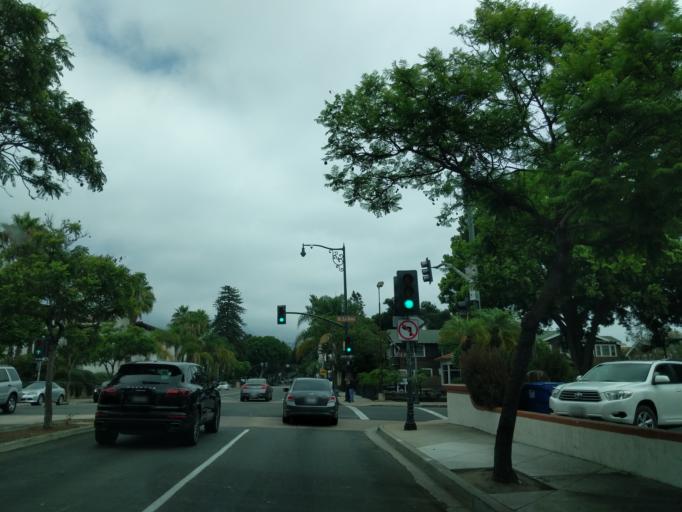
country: US
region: California
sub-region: Santa Barbara County
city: Santa Barbara
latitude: 34.4191
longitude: -119.7044
